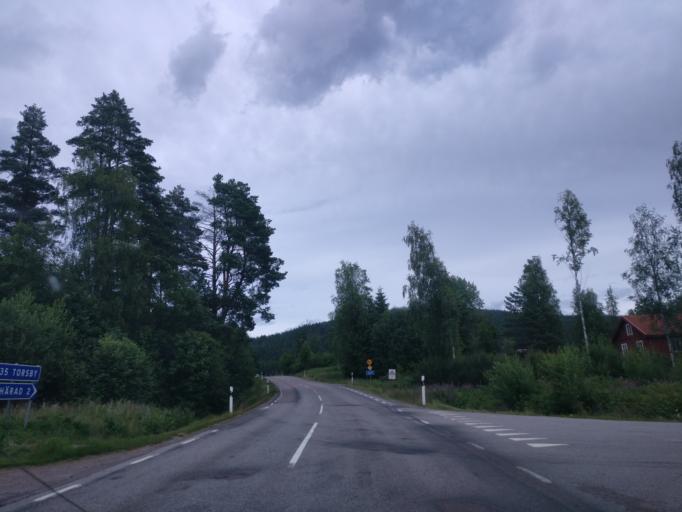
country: SE
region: Vaermland
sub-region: Hagfors Kommun
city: Ekshaerad
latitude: 60.1589
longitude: 13.4680
